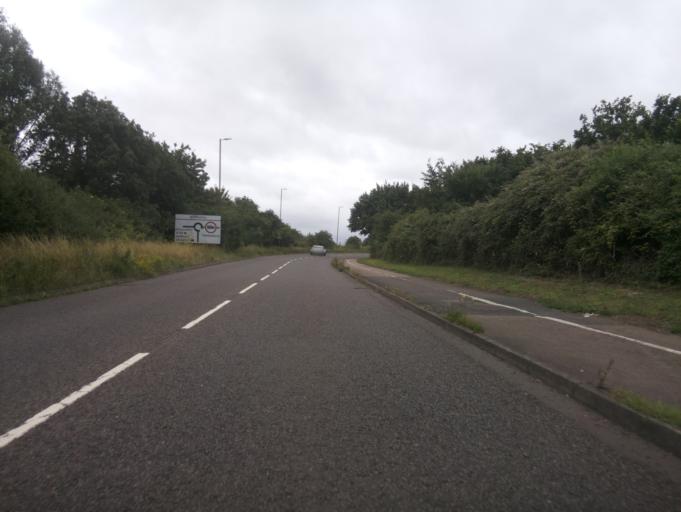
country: GB
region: England
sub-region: Gloucestershire
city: Tewkesbury
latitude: 51.9775
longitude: -2.1521
